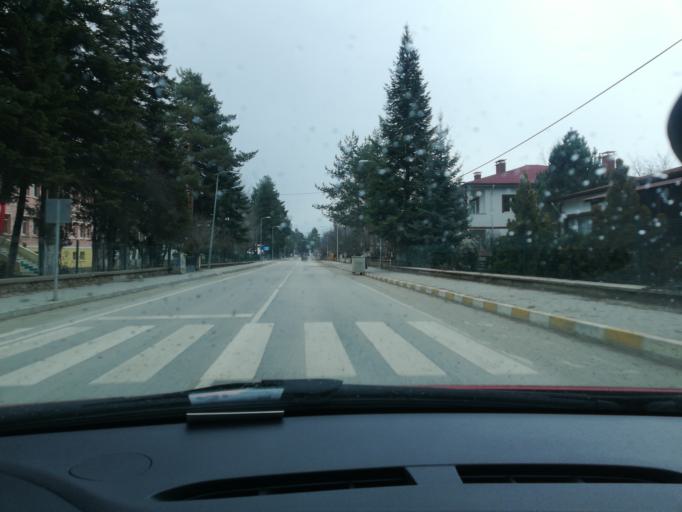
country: TR
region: Kastamonu
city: Daday
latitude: 41.4778
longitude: 33.4697
